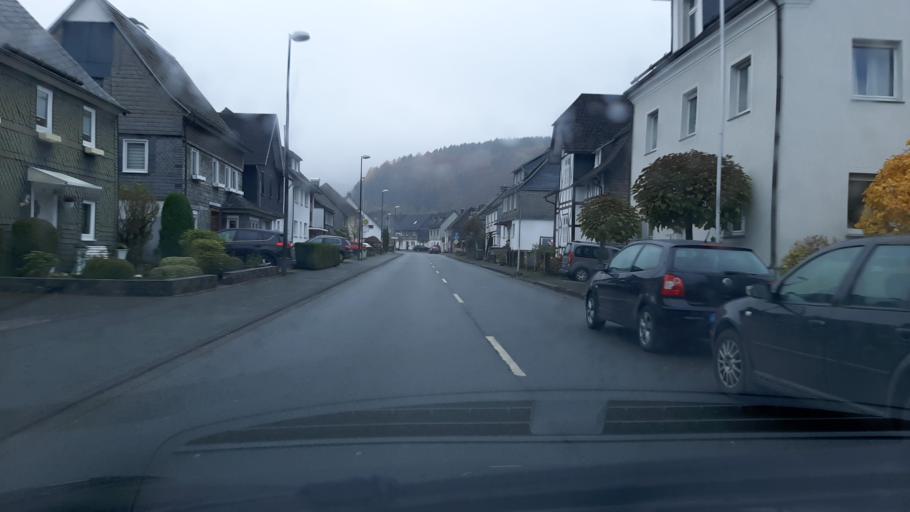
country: DE
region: North Rhine-Westphalia
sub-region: Regierungsbezirk Arnsberg
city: Winterberg
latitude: 51.2558
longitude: 8.4714
